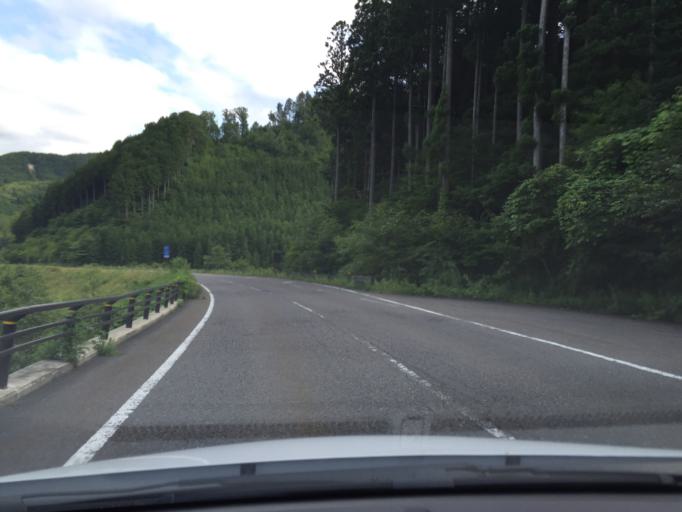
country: JP
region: Tochigi
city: Kuroiso
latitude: 37.2085
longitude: 140.0973
